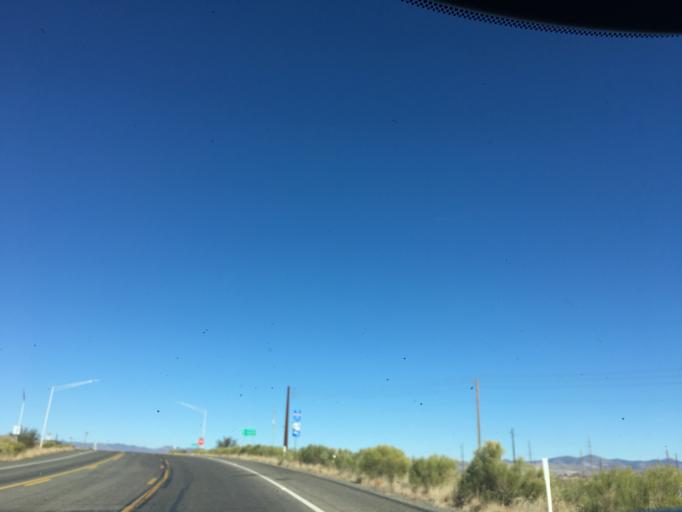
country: US
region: Arizona
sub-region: Yavapai County
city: Cordes Lakes
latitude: 34.3322
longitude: -112.1171
